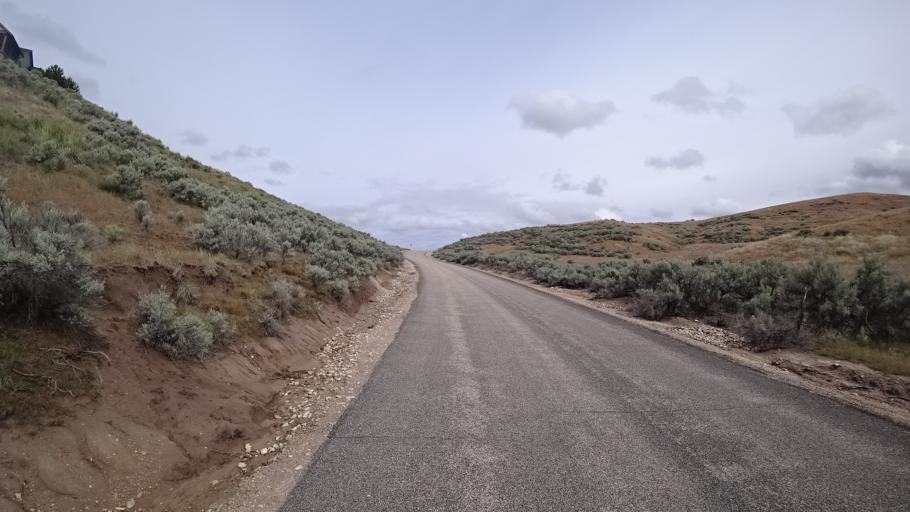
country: US
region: Idaho
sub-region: Ada County
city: Eagle
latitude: 43.7581
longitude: -116.3677
